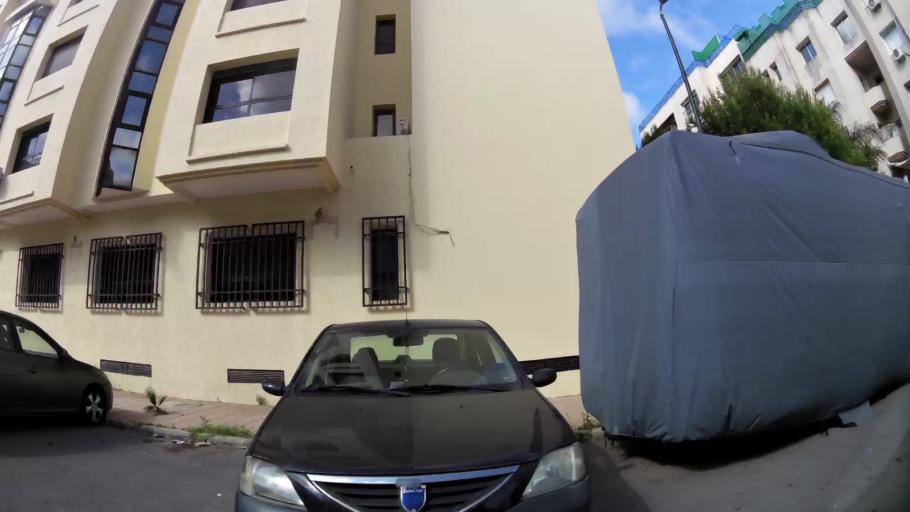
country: MA
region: Rabat-Sale-Zemmour-Zaer
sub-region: Skhirate-Temara
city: Temara
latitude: 33.9547
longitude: -6.8756
